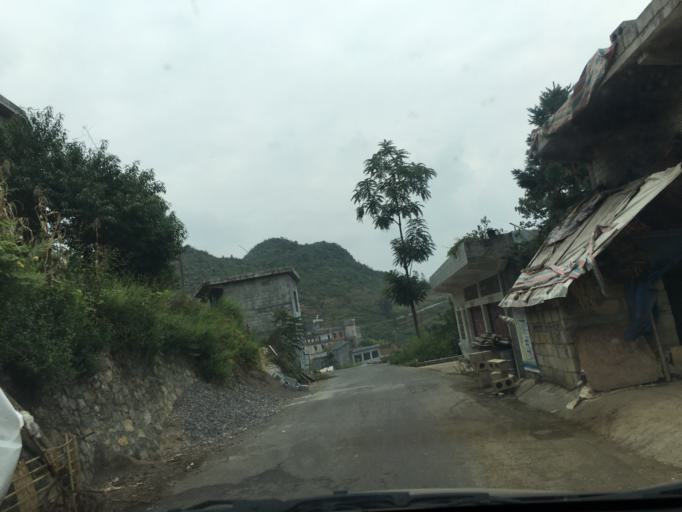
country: CN
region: Guangxi Zhuangzu Zizhiqu
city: Xinzhou
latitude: 25.5394
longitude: 105.5938
